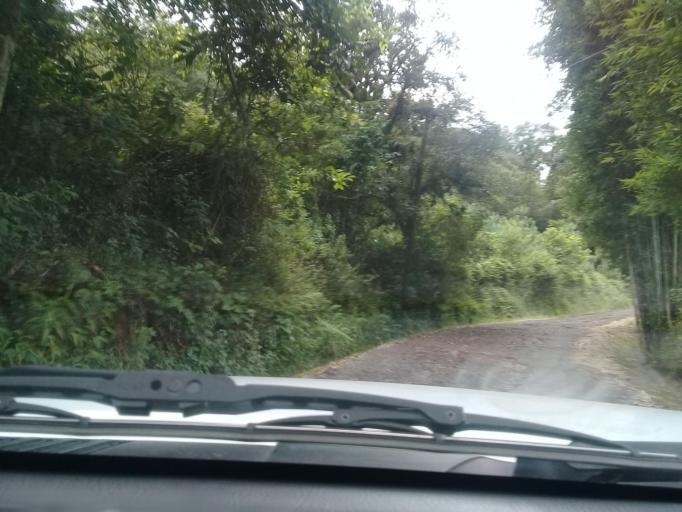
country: MX
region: Veracruz
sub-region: Rafael Lucio
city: Piletas
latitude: 19.5868
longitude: -96.9676
